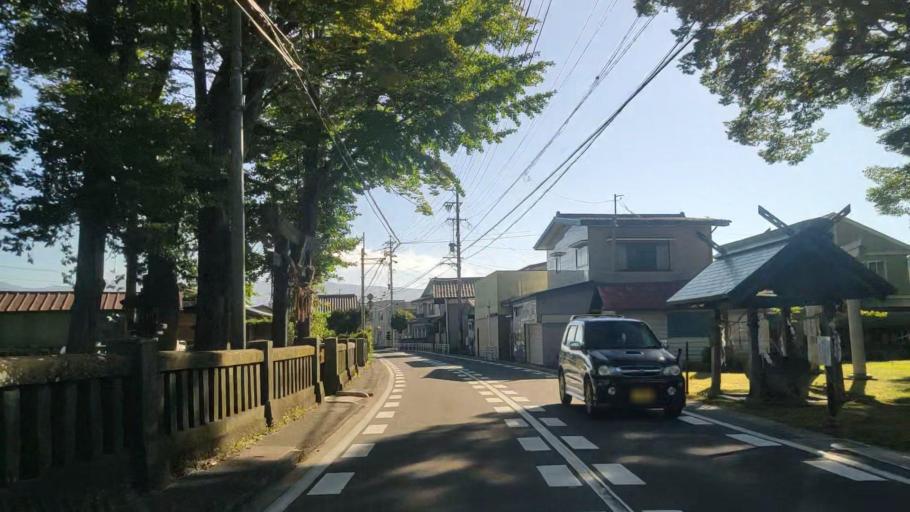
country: JP
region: Nagano
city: Okaya
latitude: 36.0543
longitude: 138.0542
